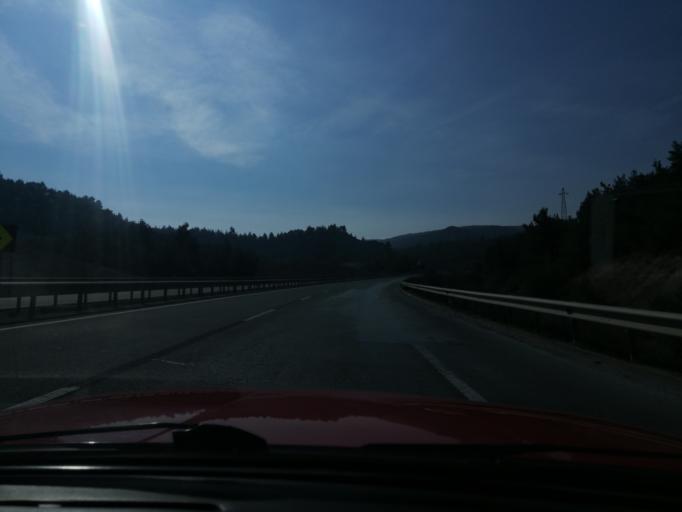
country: TR
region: Bilecik
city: Vezirhan
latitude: 40.2238
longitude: 30.0317
